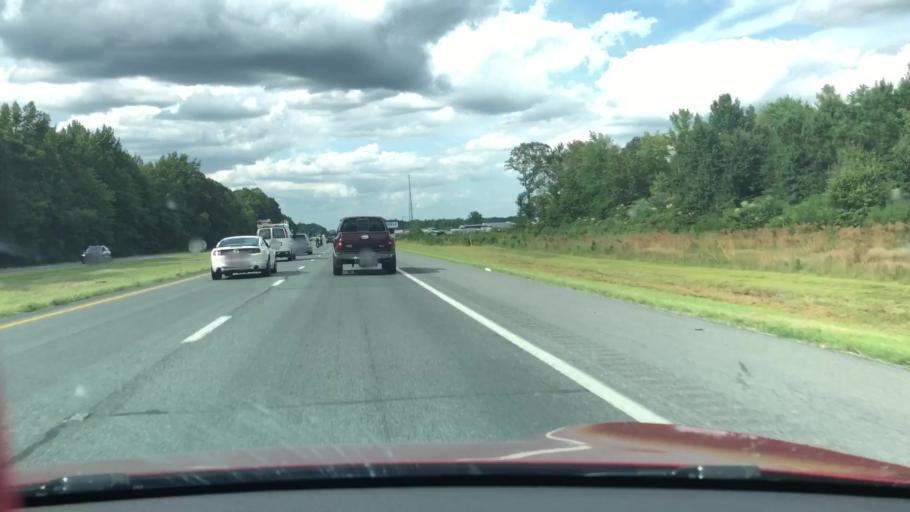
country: US
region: Delaware
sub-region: Sussex County
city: Delmar
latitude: 38.4922
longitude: -75.5574
